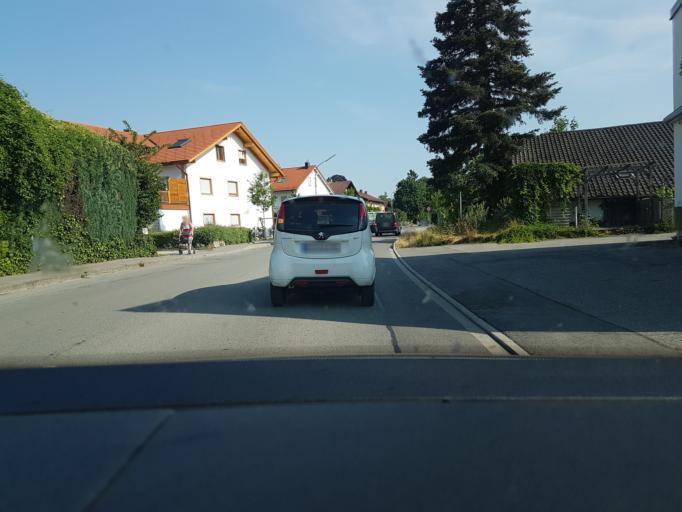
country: DE
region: Bavaria
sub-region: Upper Bavaria
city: Rosenheim
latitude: 47.8410
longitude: 12.1125
